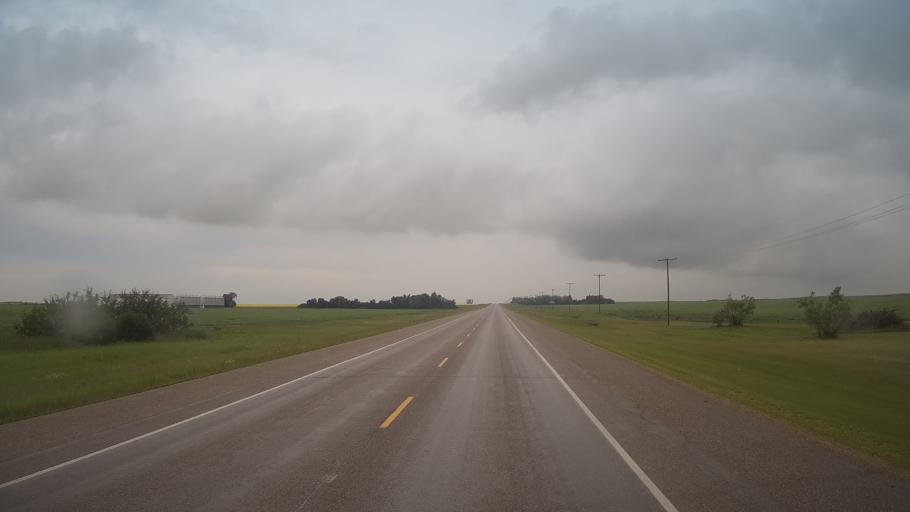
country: CA
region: Saskatchewan
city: Wilkie
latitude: 52.4057
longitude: -108.7720
